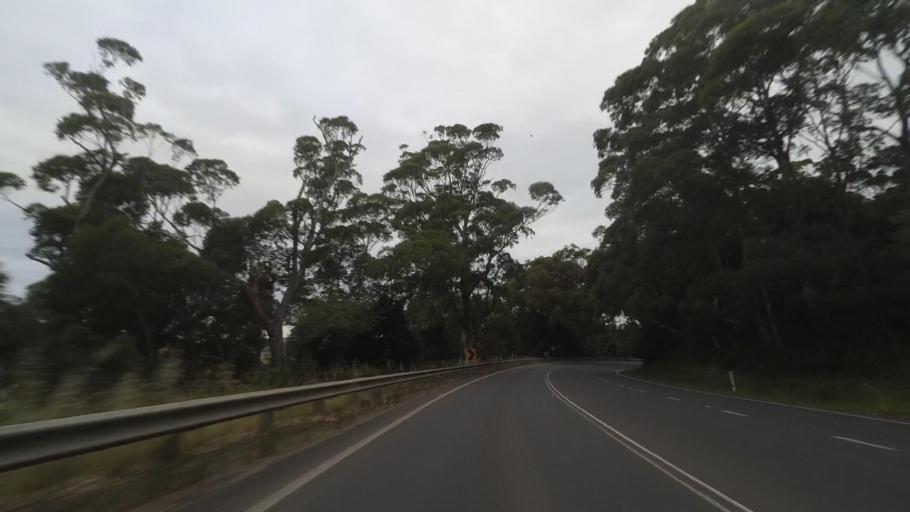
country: AU
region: New South Wales
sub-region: Kiama
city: Gerringong
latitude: -34.7427
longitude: 150.7721
